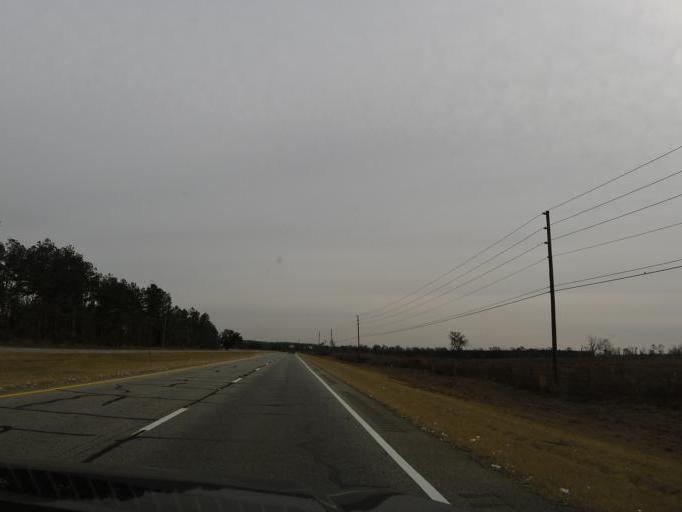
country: US
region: Georgia
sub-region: Decatur County
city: Bainbridge
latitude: 30.9480
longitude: -84.7008
